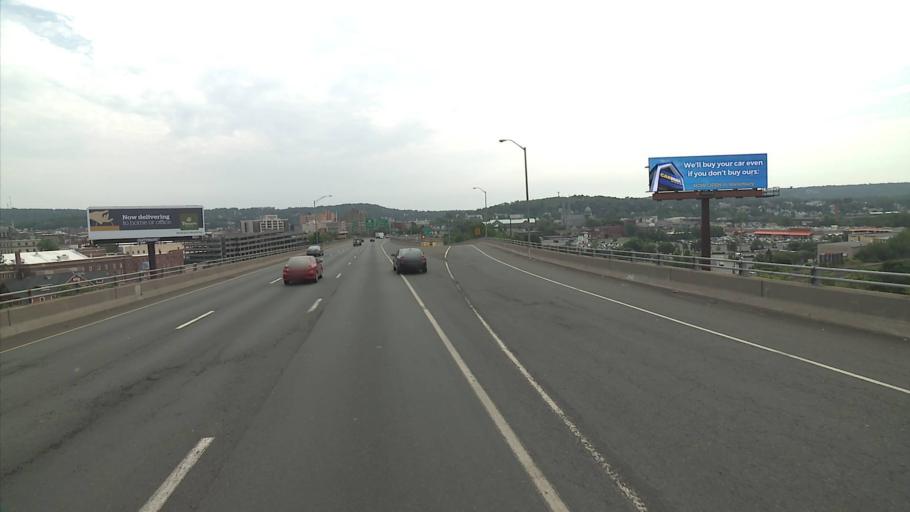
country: US
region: Connecticut
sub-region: New Haven County
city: Waterbury
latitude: 41.5518
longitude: -73.0465
